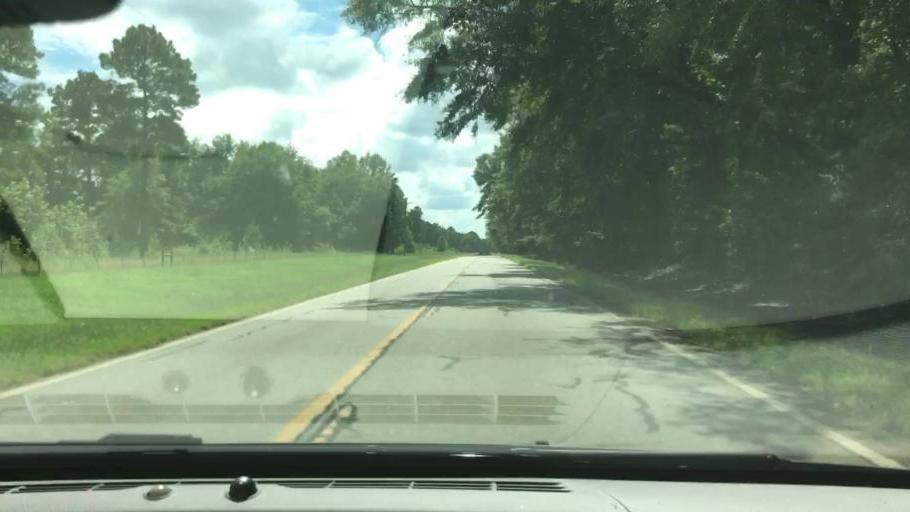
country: US
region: Georgia
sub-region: Quitman County
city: Georgetown
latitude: 32.1101
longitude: -85.0380
